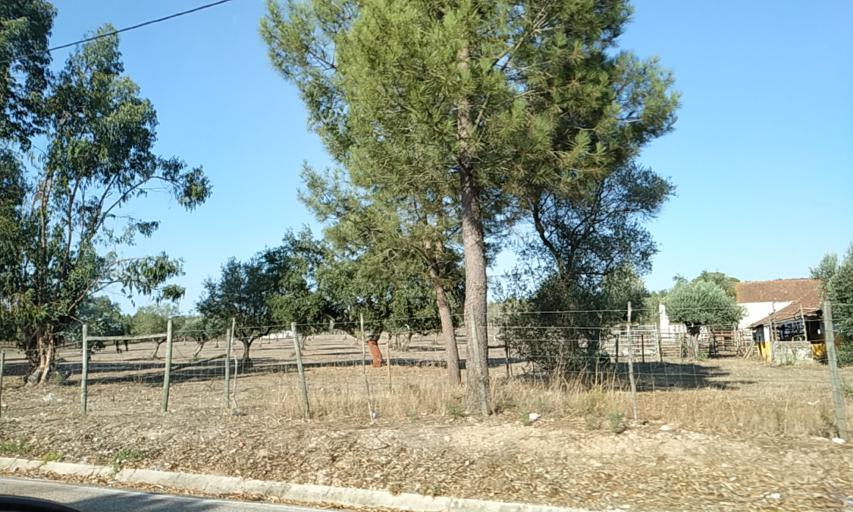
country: PT
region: Santarem
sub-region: Almeirim
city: Fazendas de Almeirim
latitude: 39.1352
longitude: -8.6100
